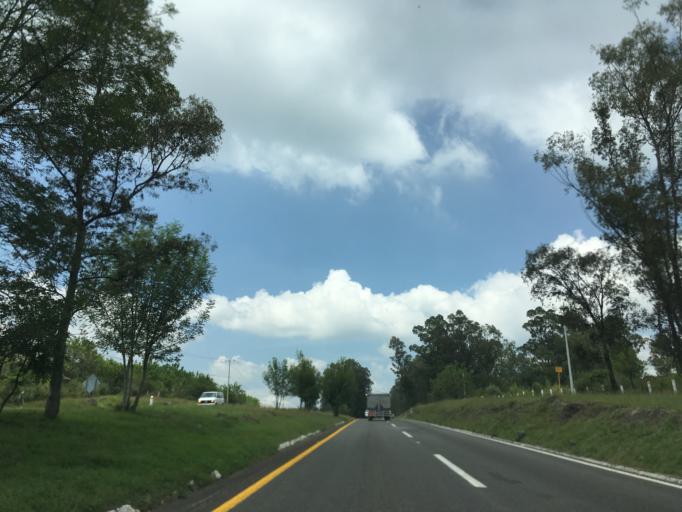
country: MX
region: Michoacan
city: Lagunillas
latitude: 19.5521
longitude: -101.3789
